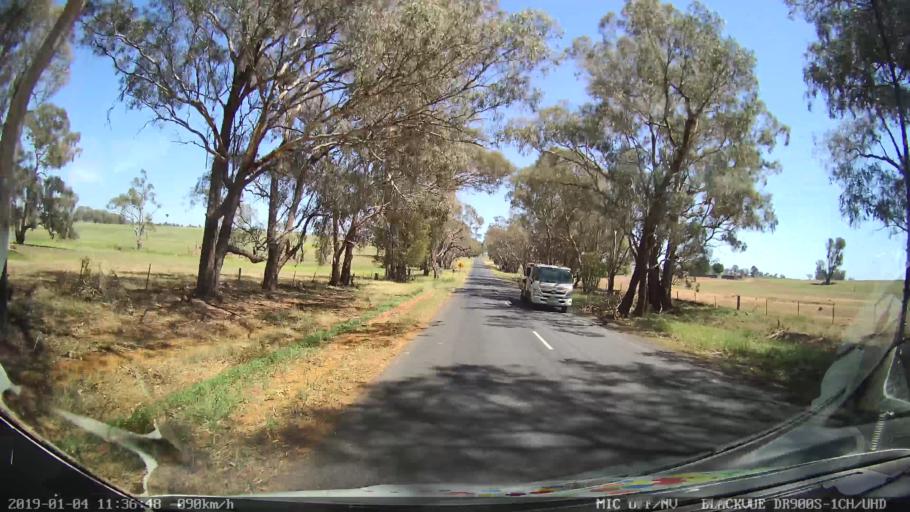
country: AU
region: New South Wales
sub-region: Cabonne
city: Molong
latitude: -33.0397
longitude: 148.8124
